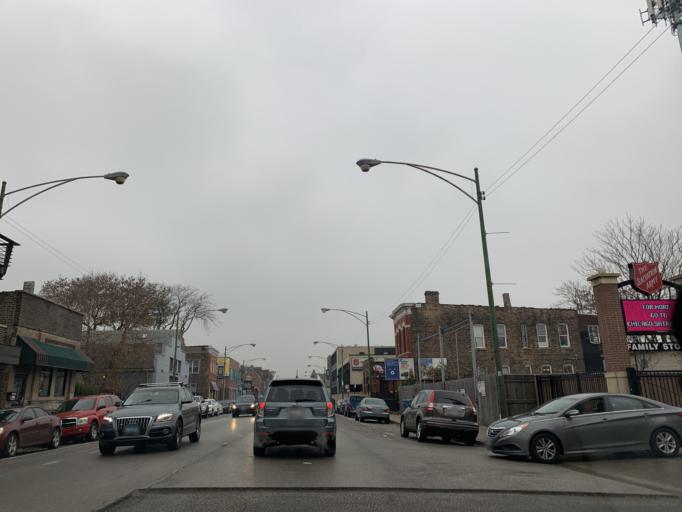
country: US
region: Illinois
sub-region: Cook County
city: Chicago
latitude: 41.9239
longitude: -87.6677
